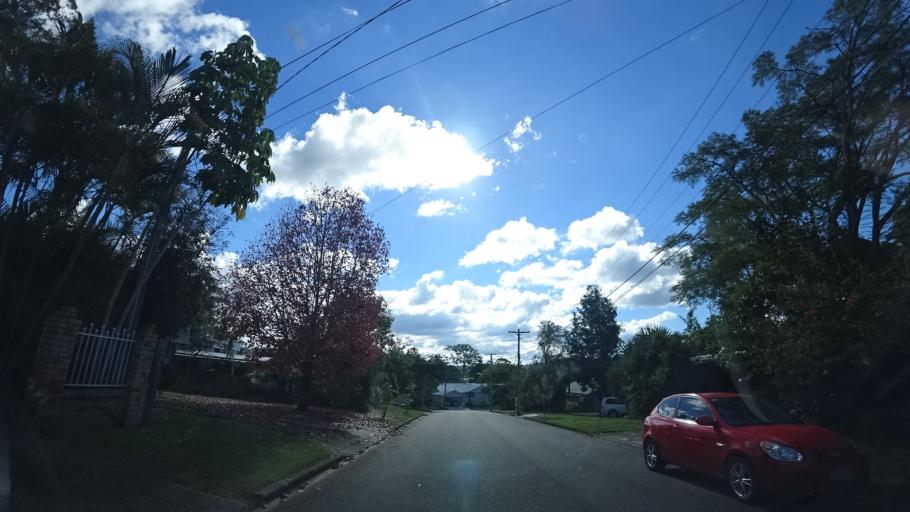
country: AU
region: Queensland
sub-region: Brisbane
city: Taringa
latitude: -27.4565
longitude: 152.9508
